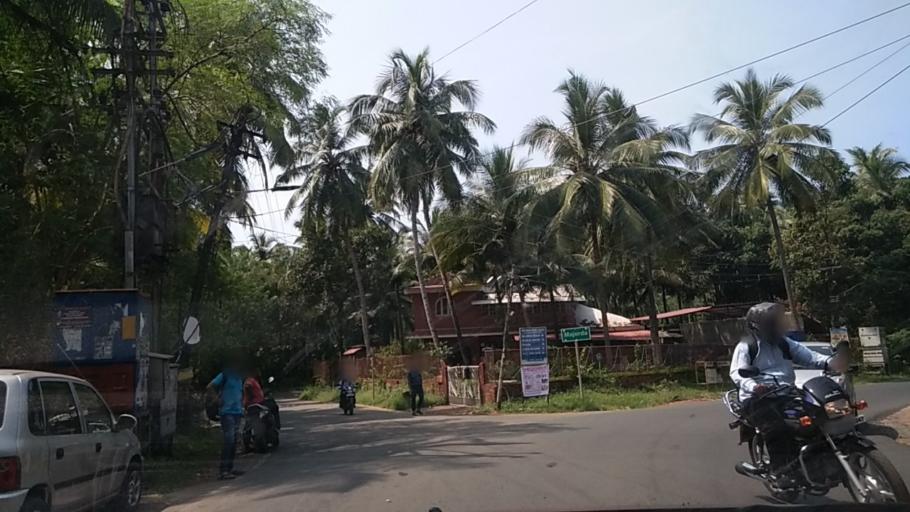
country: IN
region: Goa
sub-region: South Goa
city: Colva
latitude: 15.3133
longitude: 73.9122
